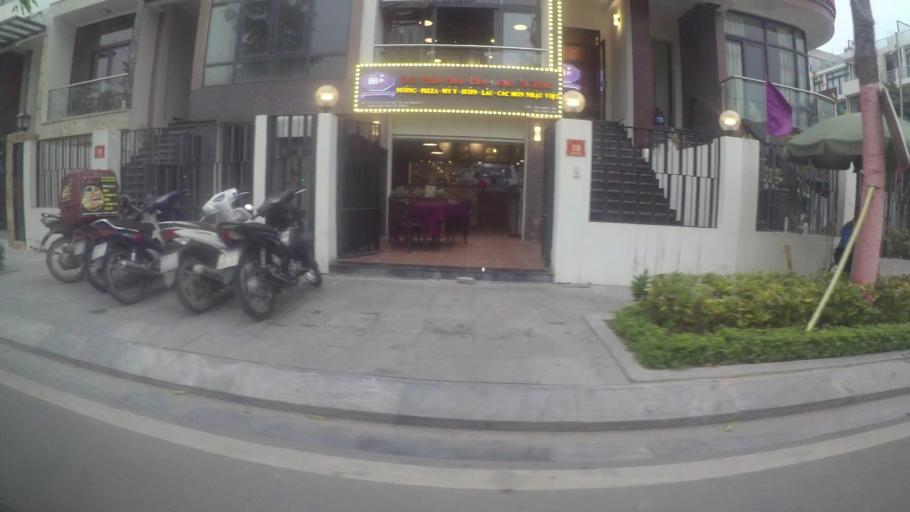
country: VN
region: Ha Noi
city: Cau Dien
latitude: 21.0349
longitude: 105.7680
